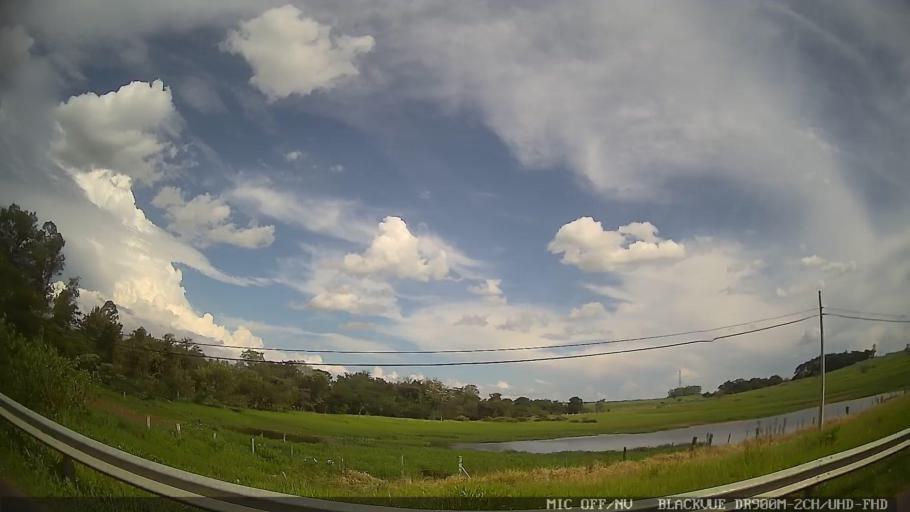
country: BR
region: Sao Paulo
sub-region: Conchas
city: Conchas
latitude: -23.0568
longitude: -47.9624
